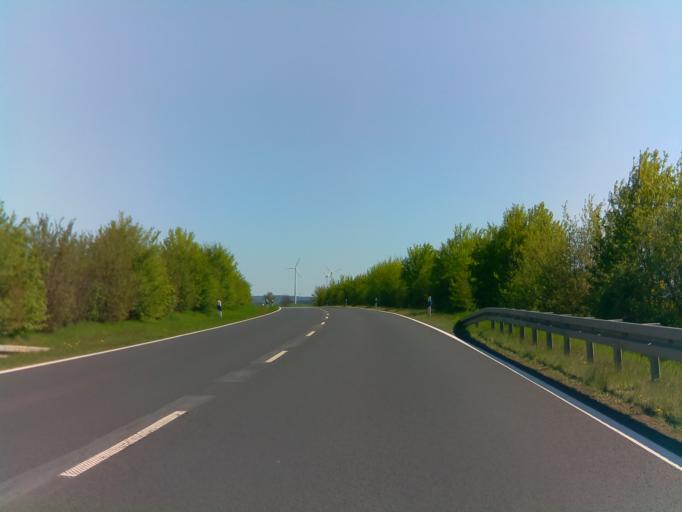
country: DE
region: Hesse
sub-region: Regierungsbezirk Giessen
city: Lauterbach
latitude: 50.6859
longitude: 9.3429
